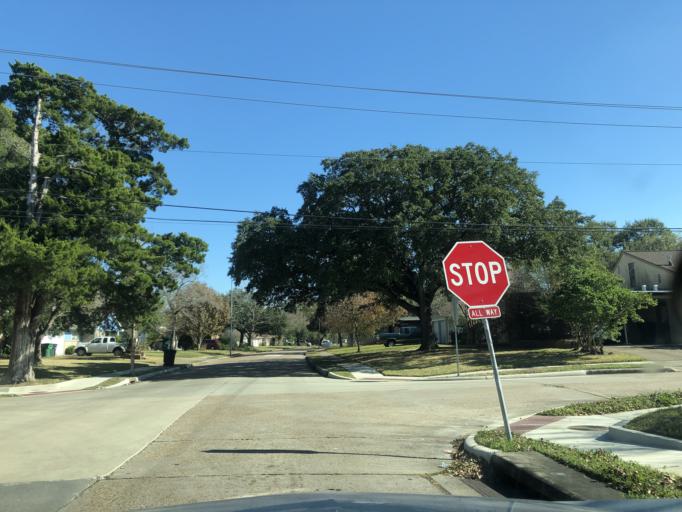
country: US
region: Texas
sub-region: Harris County
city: Bellaire
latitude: 29.6988
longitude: -95.5084
